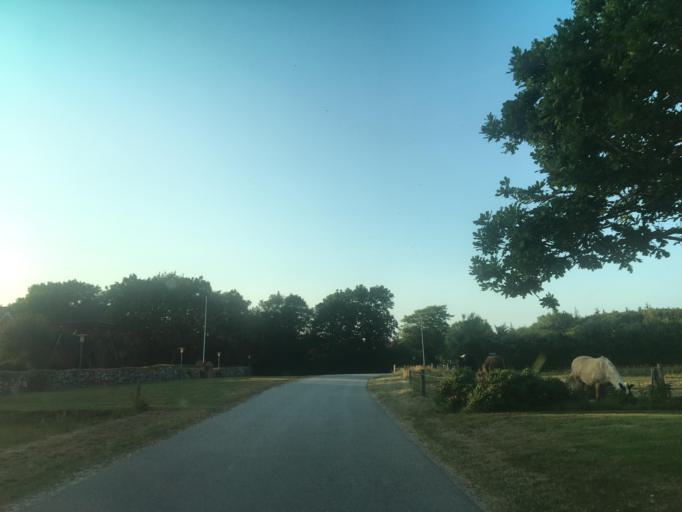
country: DK
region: North Denmark
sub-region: Thisted Kommune
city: Hurup
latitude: 56.8509
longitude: 8.3645
